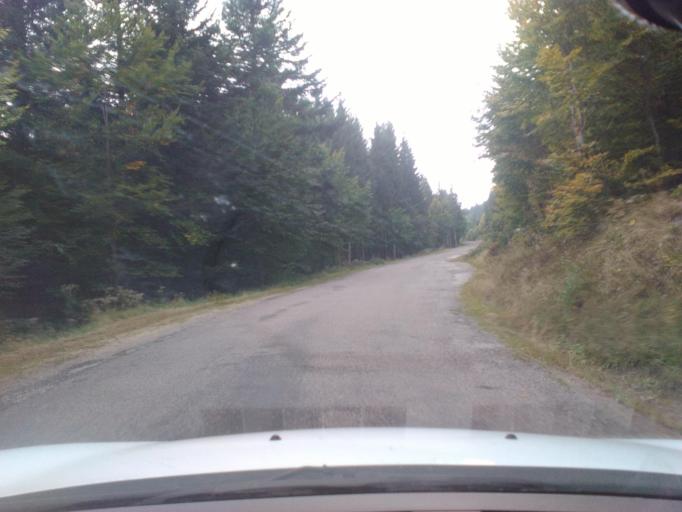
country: FR
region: Lorraine
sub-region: Departement des Vosges
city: Gerardmer
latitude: 48.0434
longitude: 6.9044
